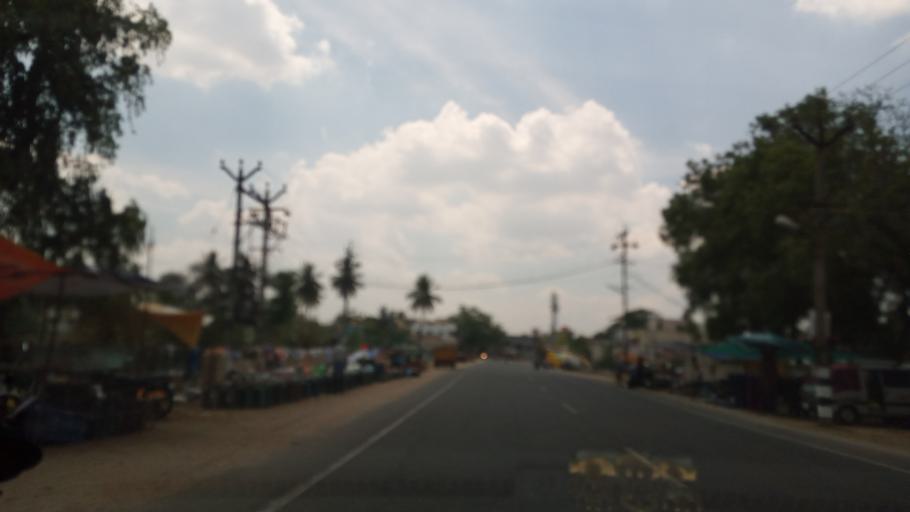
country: IN
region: Tamil Nadu
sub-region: Vellore
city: Walajapet
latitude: 12.9236
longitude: 79.3733
